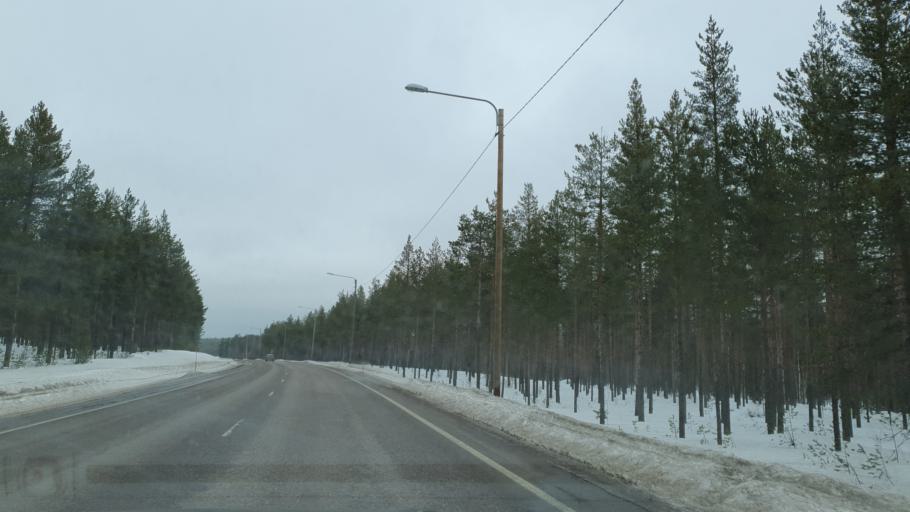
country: FI
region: Lapland
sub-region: Torniolaakso
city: Pello
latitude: 66.9078
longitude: 24.0973
